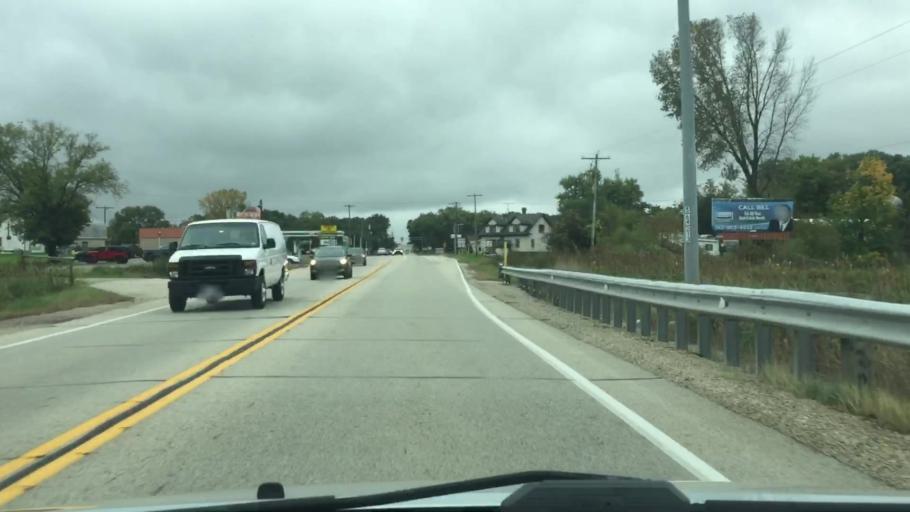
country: US
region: Wisconsin
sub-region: Walworth County
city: Elkhorn
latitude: 42.7272
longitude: -88.5428
